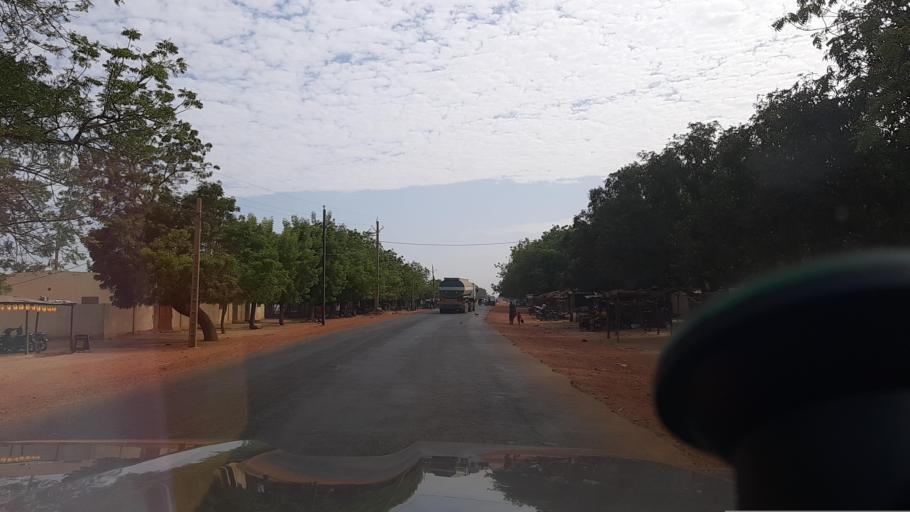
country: ML
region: Segou
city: Segou
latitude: 13.4950
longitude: -6.1717
